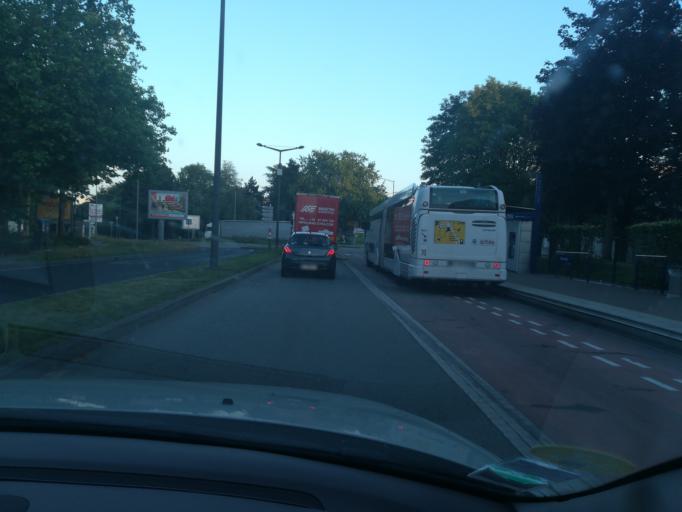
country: FR
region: Haute-Normandie
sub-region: Departement de la Seine-Maritime
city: Bois-Guillaume
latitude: 49.4623
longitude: 1.1314
